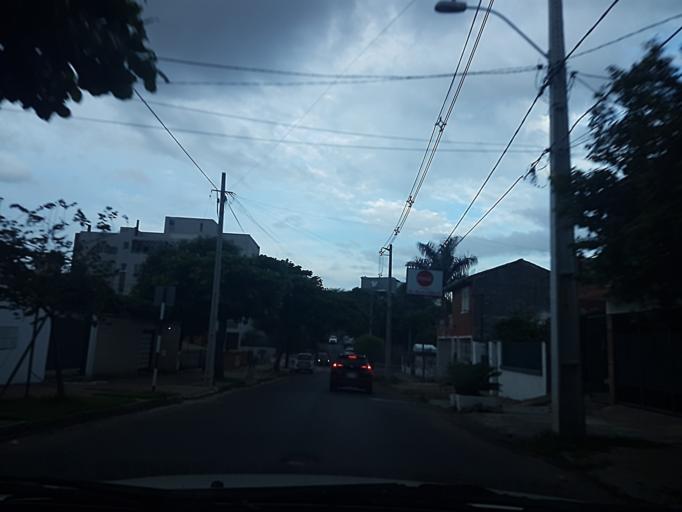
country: PY
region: Asuncion
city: Asuncion
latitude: -25.2771
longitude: -57.6015
